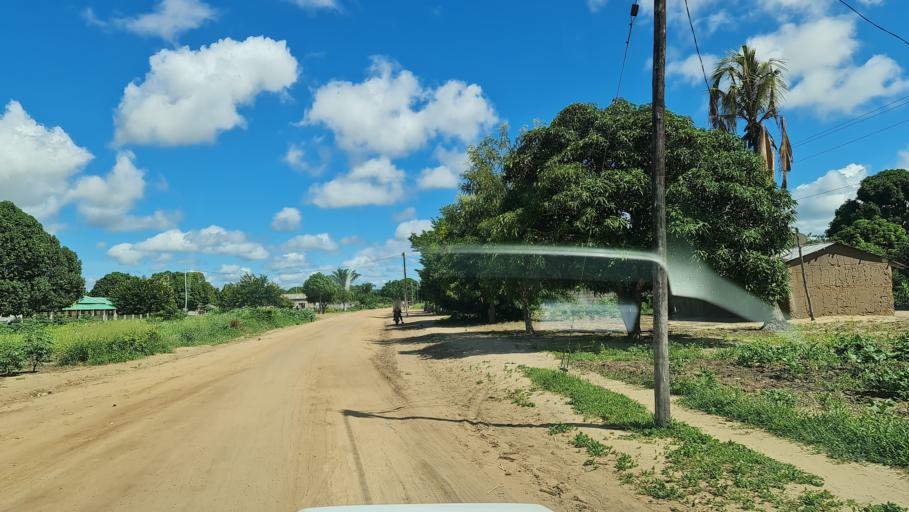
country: MZ
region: Nampula
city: Ilha de Mocambique
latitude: -15.5549
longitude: 40.4102
